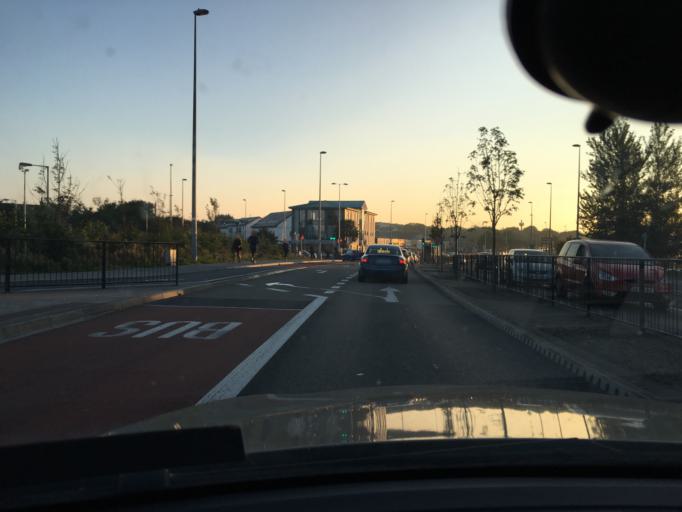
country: IE
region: Connaught
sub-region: County Galway
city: Gaillimh
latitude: 53.2765
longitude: -9.0735
